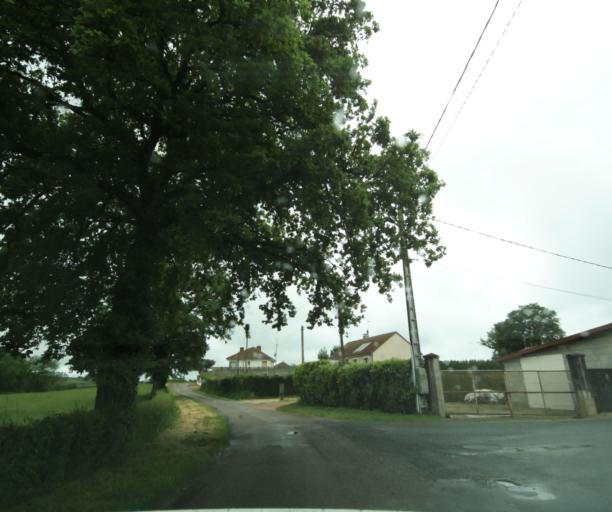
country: FR
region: Bourgogne
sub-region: Departement de Saone-et-Loire
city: Charolles
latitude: 46.4800
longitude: 4.4364
